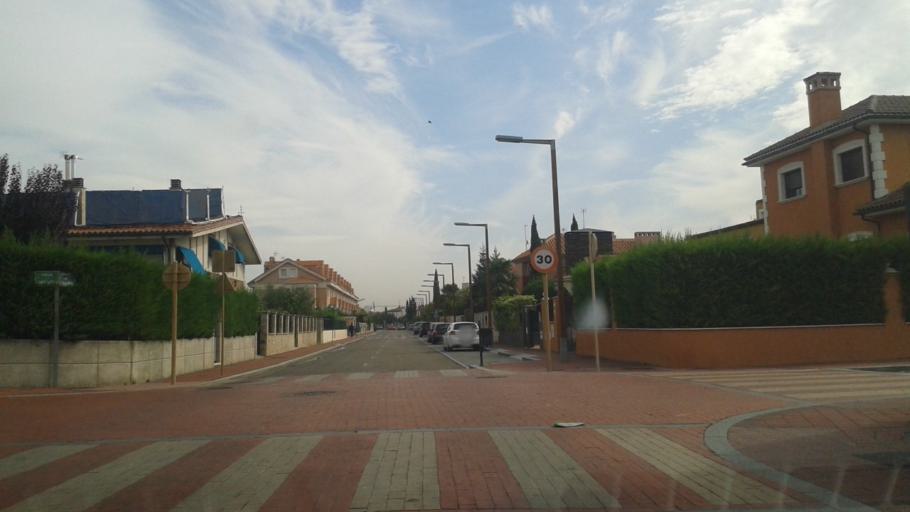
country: ES
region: Castille and Leon
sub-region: Provincia de Valladolid
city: Arroyo
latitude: 41.6096
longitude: -4.7899
